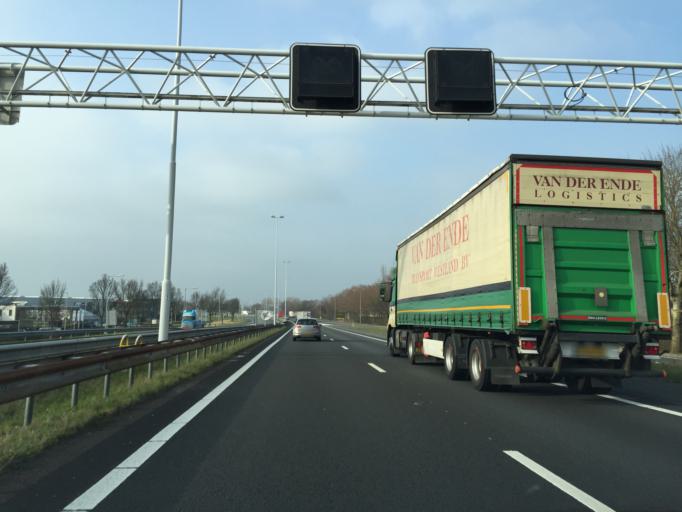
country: NL
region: South Holland
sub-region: Gemeente Westland
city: Maasdijk
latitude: 51.9543
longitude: 4.2318
